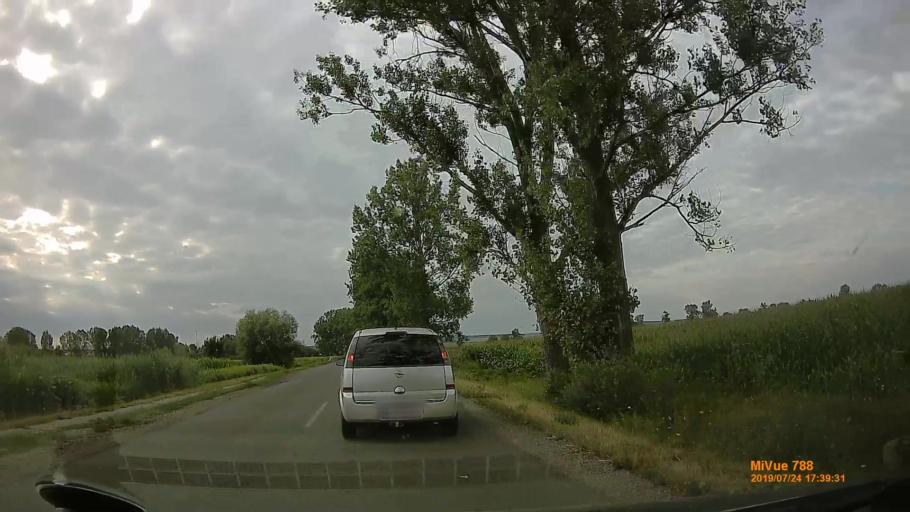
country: HU
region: Borsod-Abauj-Zemplen
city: Encs
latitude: 48.3274
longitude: 21.1433
